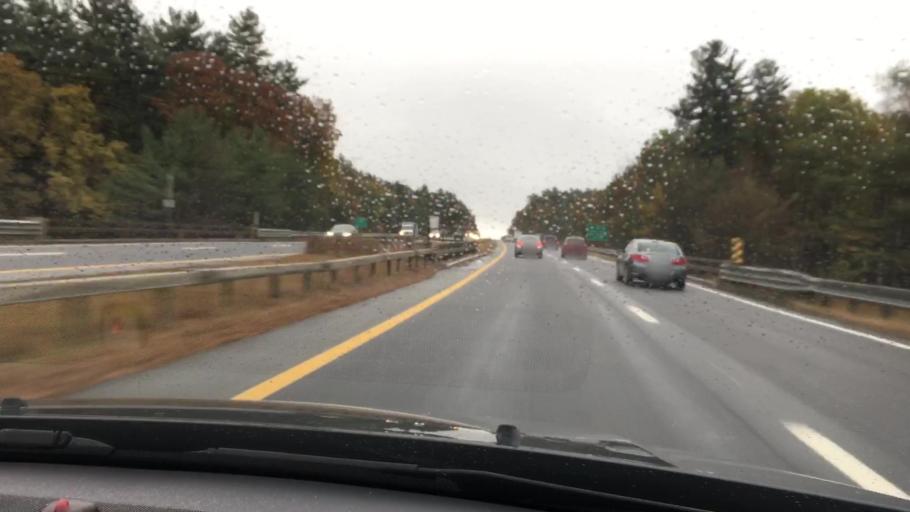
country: US
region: New Hampshire
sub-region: Hillsborough County
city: Litchfield
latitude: 42.8049
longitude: -71.4990
